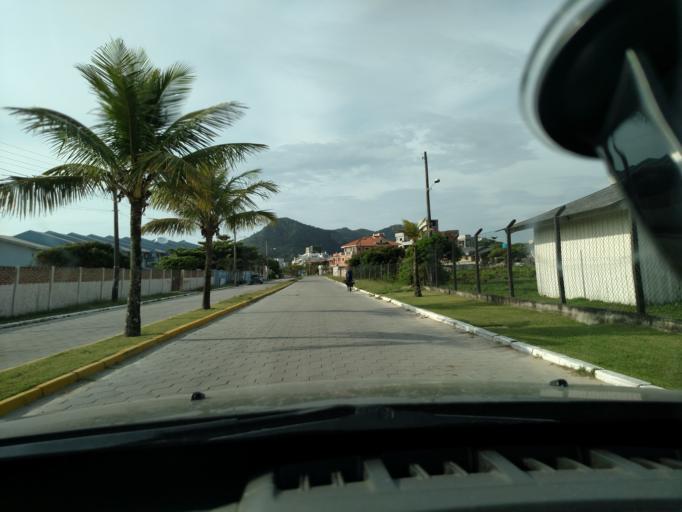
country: BR
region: Santa Catarina
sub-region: Porto Belo
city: Porto Belo
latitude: -27.1874
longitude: -48.5001
